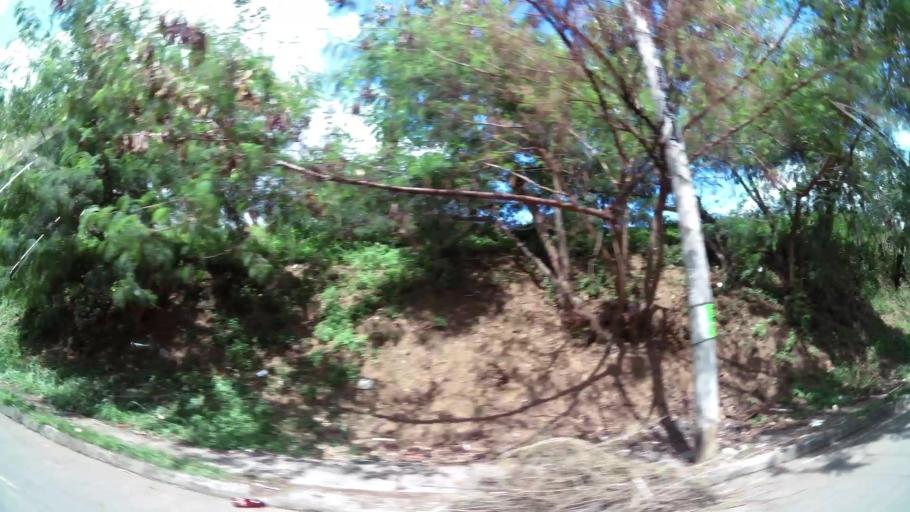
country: CO
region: Valle del Cauca
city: Cali
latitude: 3.3997
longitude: -76.5197
